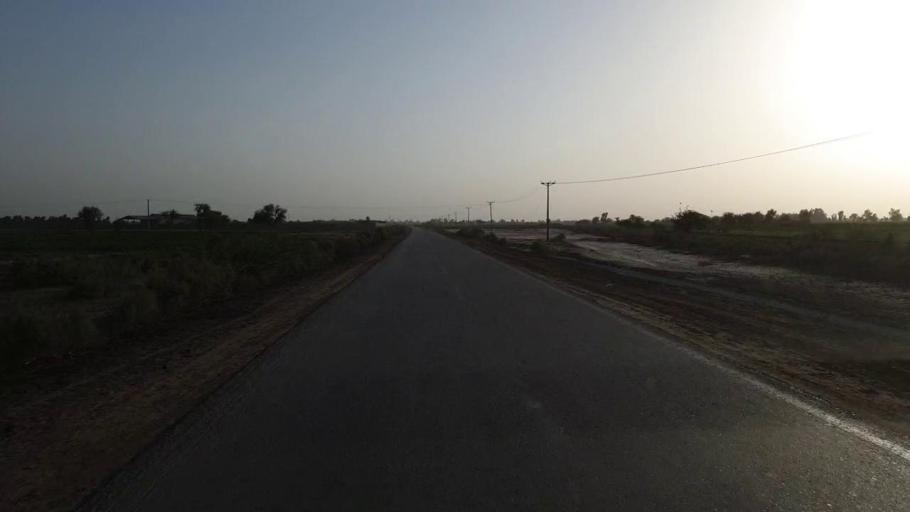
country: PK
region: Sindh
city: Jam Sahib
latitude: 26.2824
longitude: 68.5826
